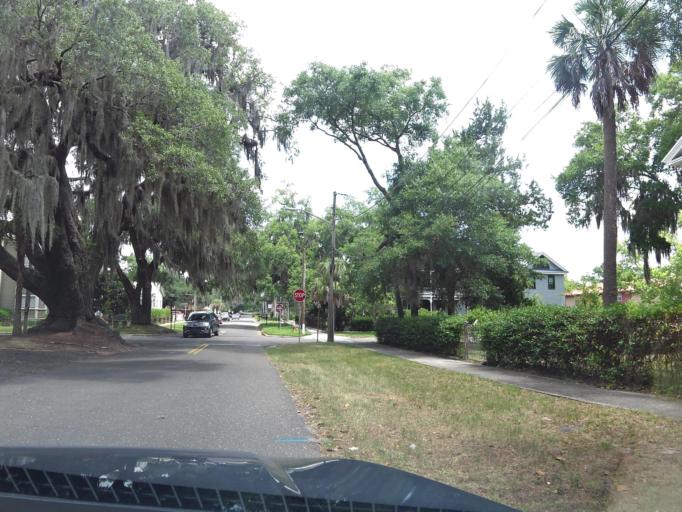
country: US
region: Florida
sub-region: Nassau County
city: Fernandina Beach
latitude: 30.6689
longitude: -81.4574
